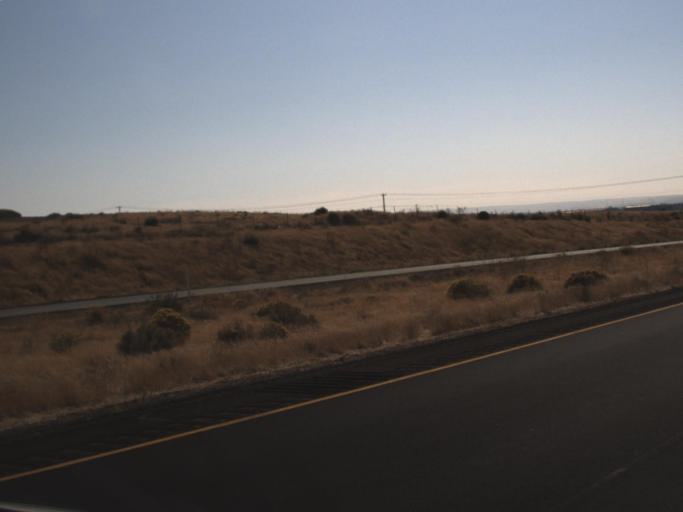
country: US
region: Washington
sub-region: Franklin County
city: Pasco
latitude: 46.2871
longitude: -119.0939
